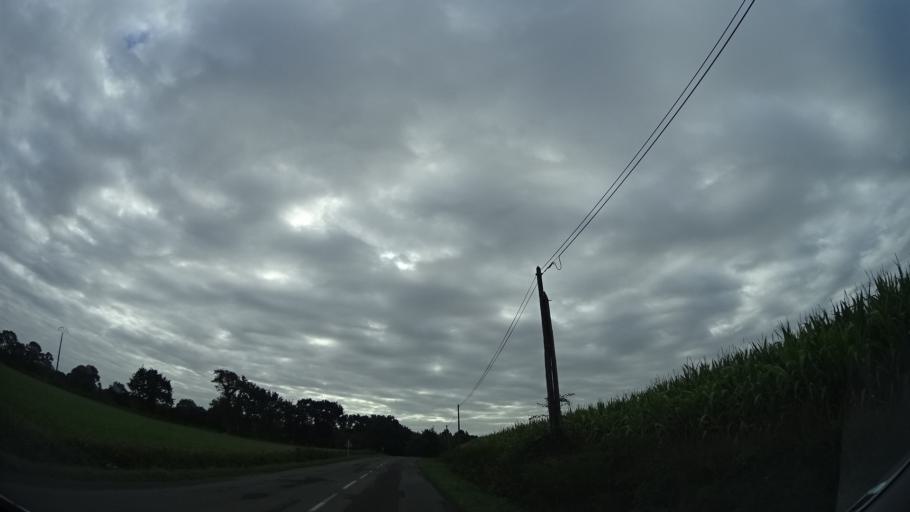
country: FR
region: Brittany
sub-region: Departement d'Ille-et-Vilaine
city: Montreuil-sur-Ille
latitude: 48.3382
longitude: -1.6538
